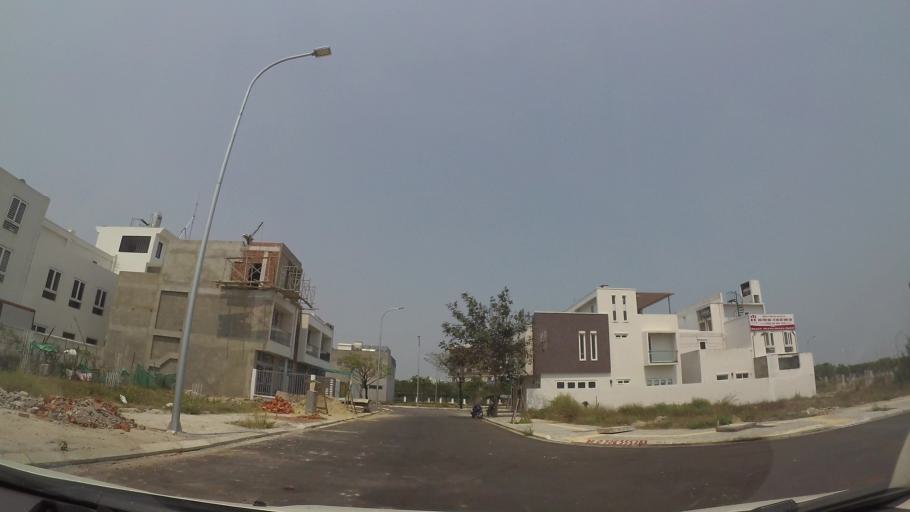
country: VN
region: Da Nang
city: Ngu Hanh Son
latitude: 15.9771
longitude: 108.2614
